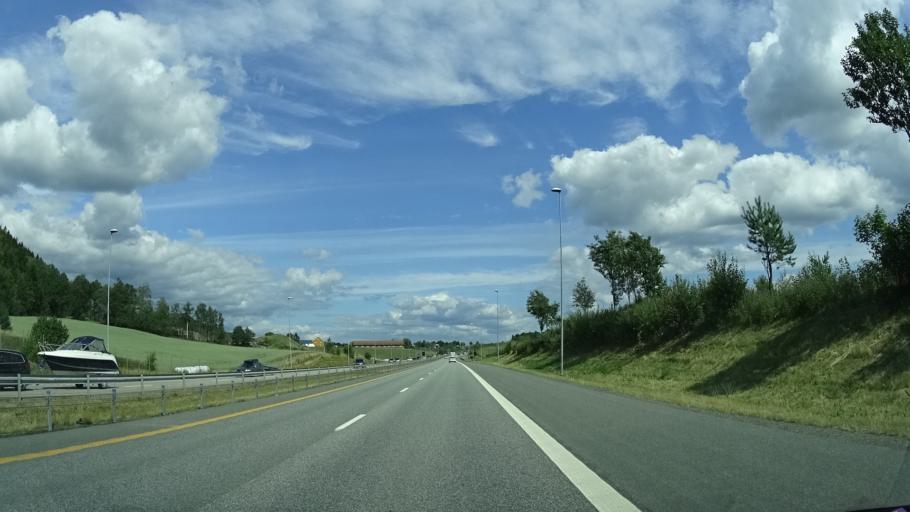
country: NO
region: Vestfold
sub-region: Sande
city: Sande
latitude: 59.6300
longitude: 10.2035
